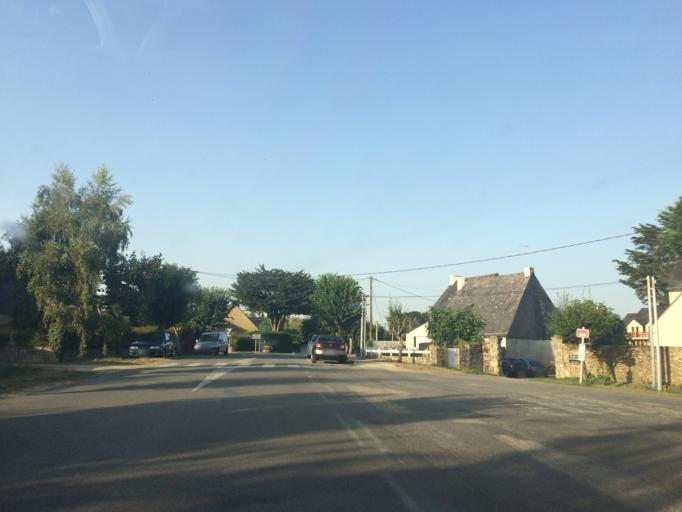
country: FR
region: Brittany
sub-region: Departement du Morbihan
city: Damgan
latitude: 47.5151
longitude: -2.5536
